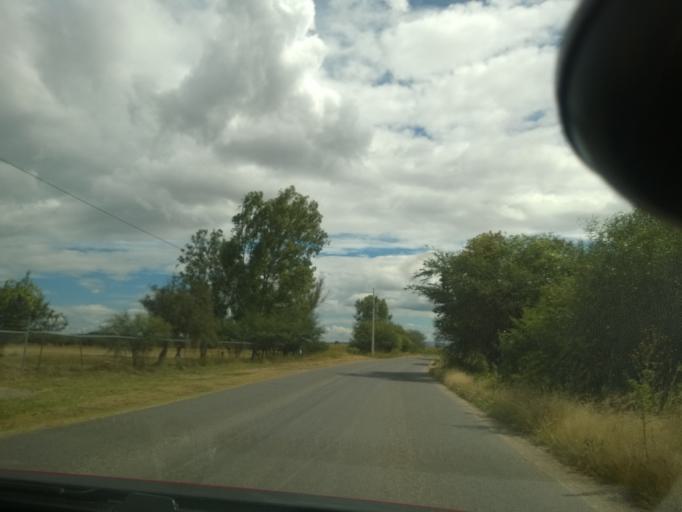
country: MX
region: Guanajuato
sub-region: Leon
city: Plan Guanajuato (La Sandia)
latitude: 20.9614
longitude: -101.6350
